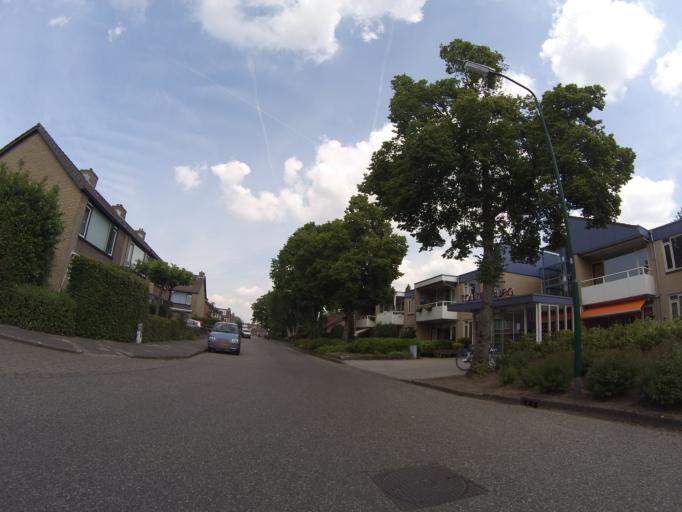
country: NL
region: Utrecht
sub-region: Gemeente De Bilt
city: De Bilt
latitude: 52.1528
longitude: 5.1731
